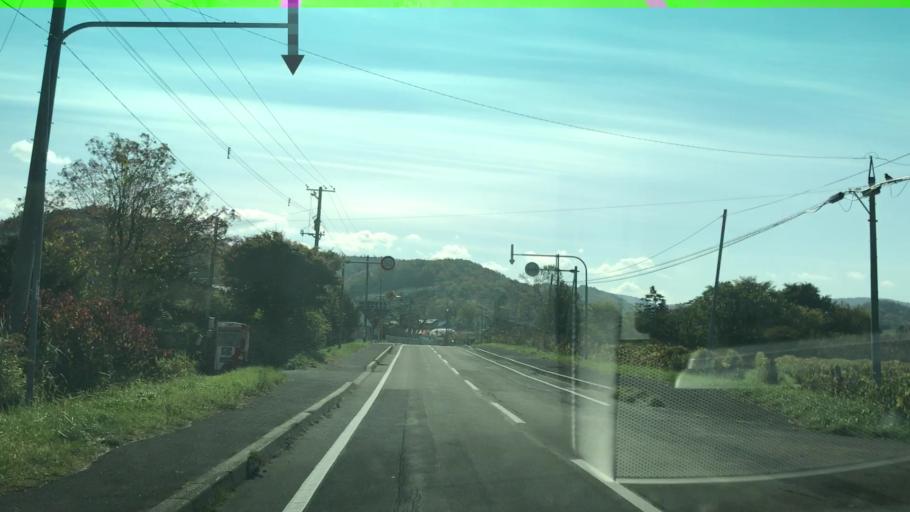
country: JP
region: Hokkaido
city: Yoichi
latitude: 43.1682
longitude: 140.8209
